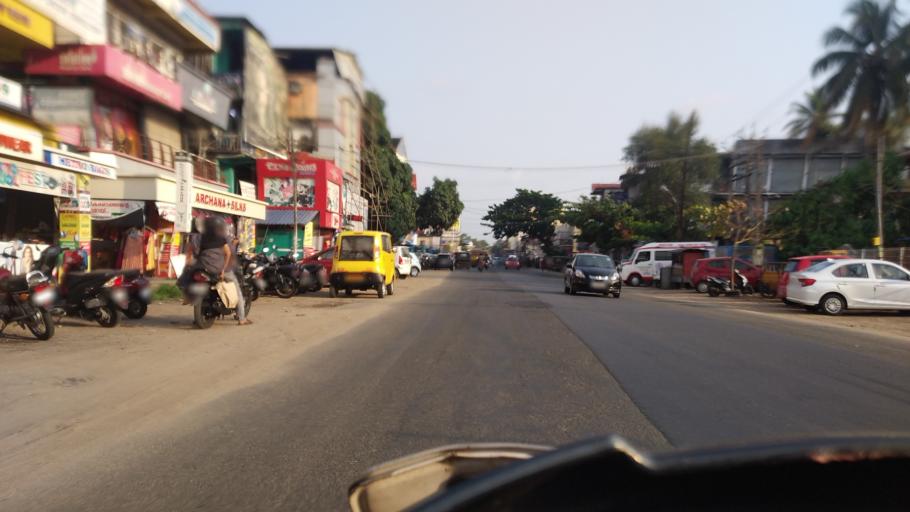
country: IN
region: Kerala
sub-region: Thrissur District
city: Thanniyam
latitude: 10.4160
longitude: 76.1067
